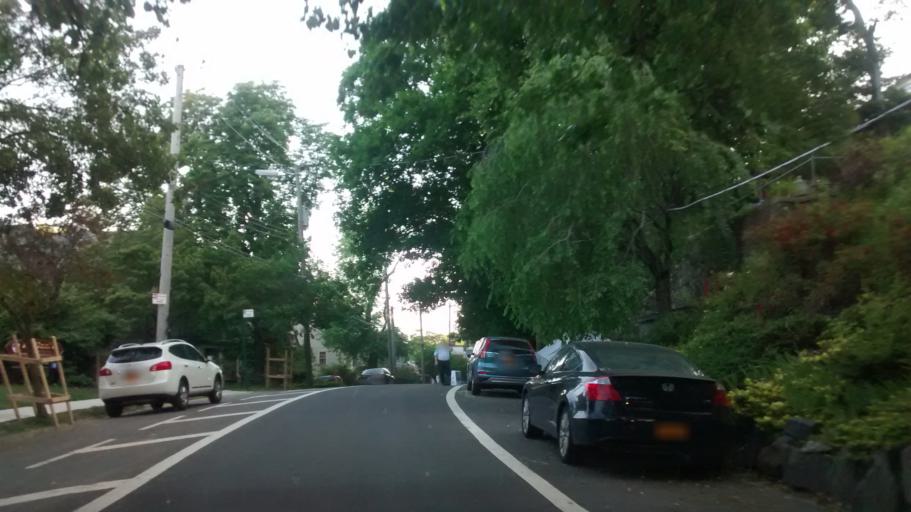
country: US
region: New Jersey
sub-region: Hudson County
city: Bayonne
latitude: 40.6325
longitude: -74.0792
